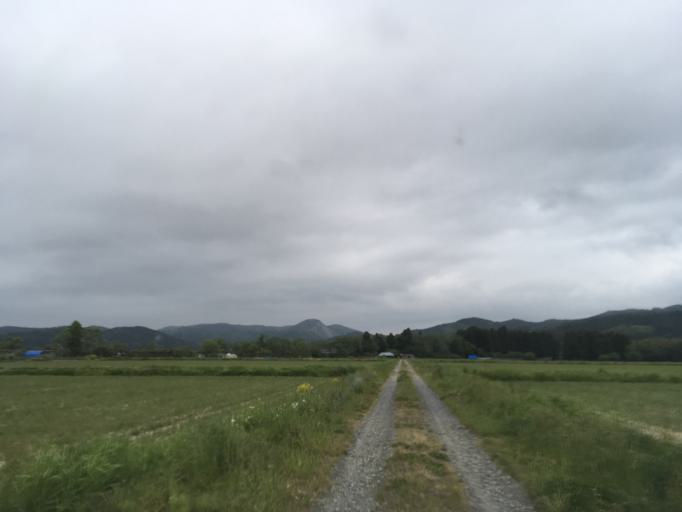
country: JP
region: Miyagi
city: Wakuya
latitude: 38.7161
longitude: 141.2861
